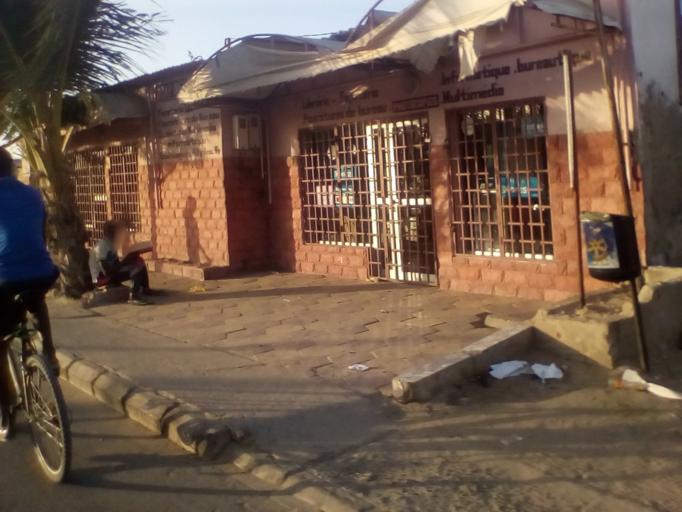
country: SN
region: Saint-Louis
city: Saint-Louis
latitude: 16.0204
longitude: -16.4979
